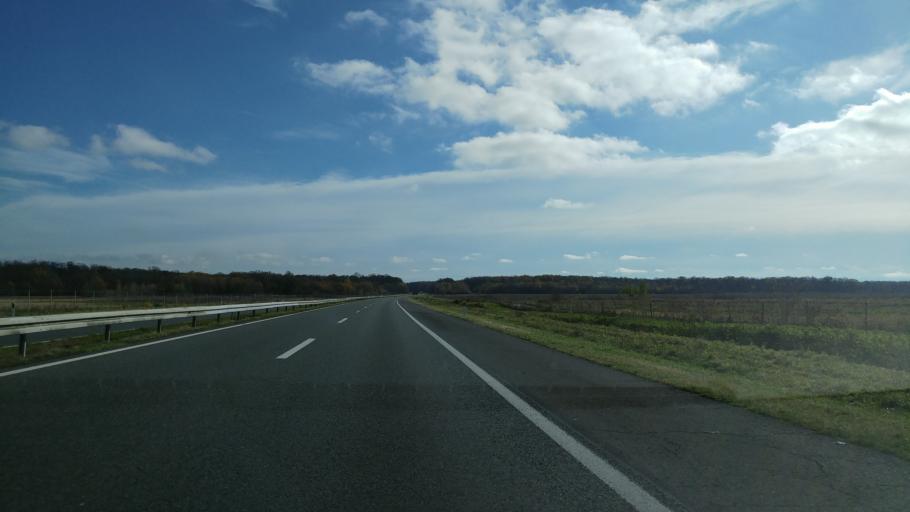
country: HR
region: Sisacko-Moslavacka
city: Lipovljani
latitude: 45.3537
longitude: 16.9094
